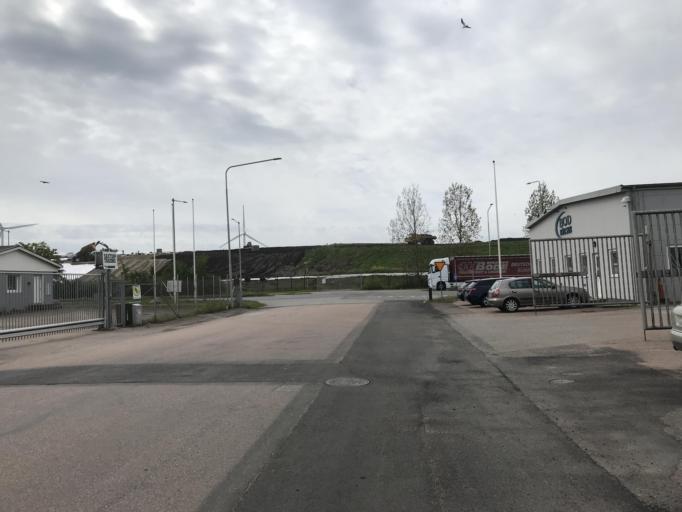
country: SE
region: Skane
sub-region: Landskrona
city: Landskrona
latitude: 55.8658
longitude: 12.8623
